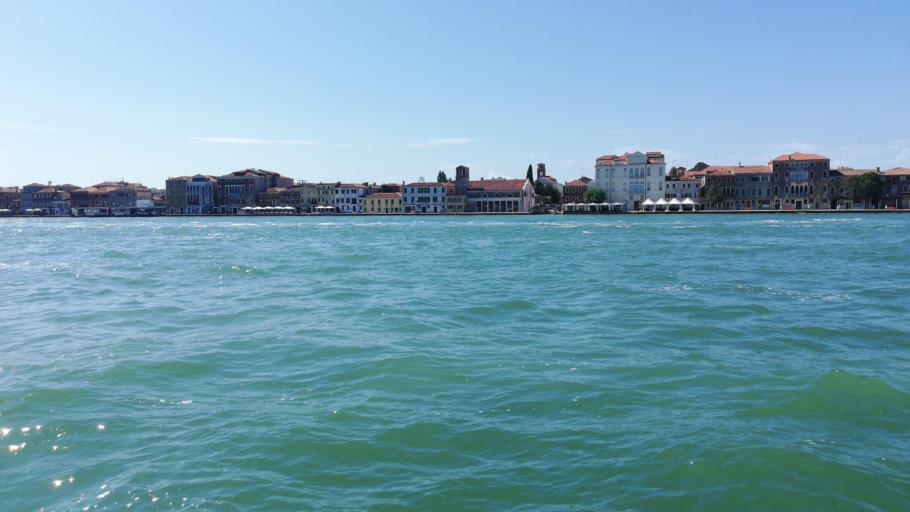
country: IT
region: Veneto
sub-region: Provincia di Venezia
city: Giudecca
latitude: 45.4293
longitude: 12.3240
